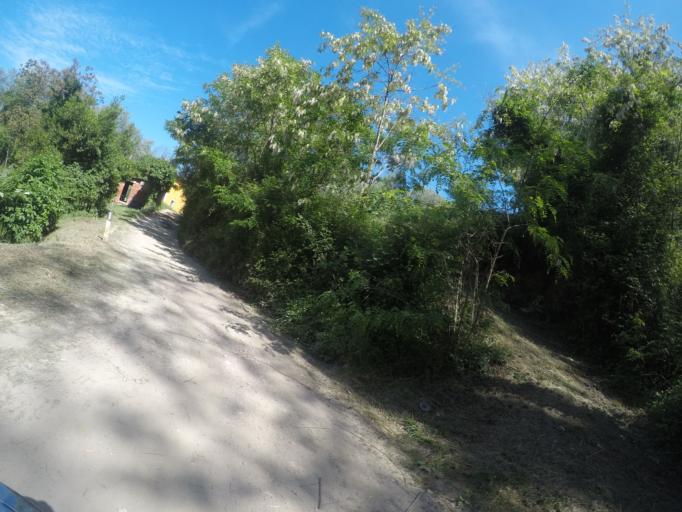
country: IT
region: Tuscany
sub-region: Provincia di Massa-Carrara
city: Massa
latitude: 44.0639
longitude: 10.1059
